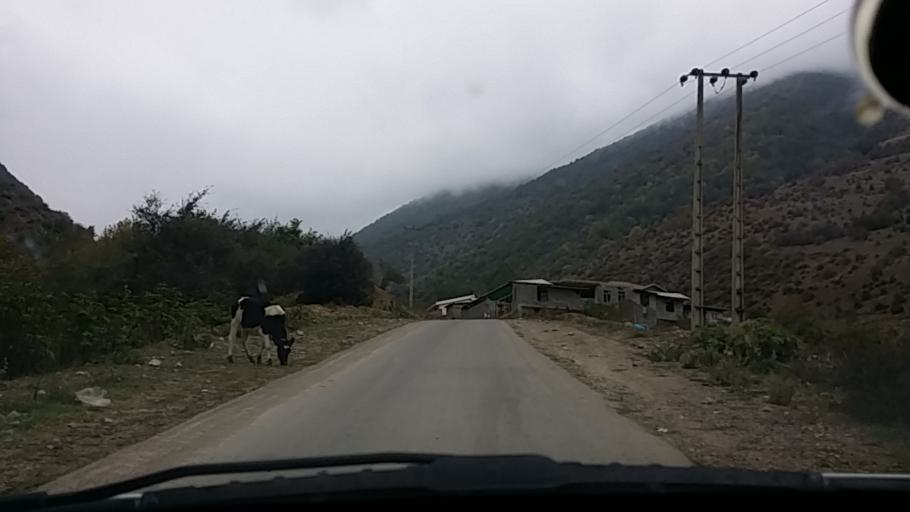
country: IR
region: Mazandaran
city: `Abbasabad
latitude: 36.4654
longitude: 51.1386
